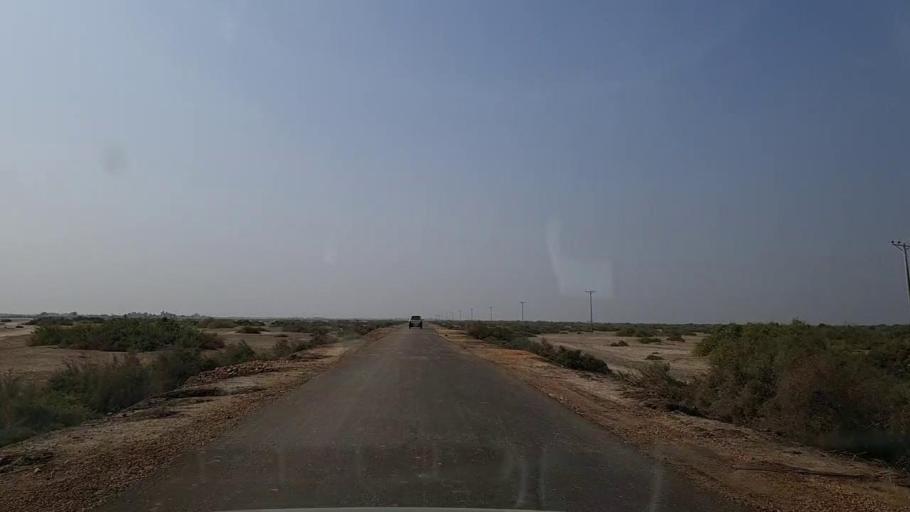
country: PK
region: Sindh
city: Mirpur Sakro
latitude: 24.5289
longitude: 67.5870
